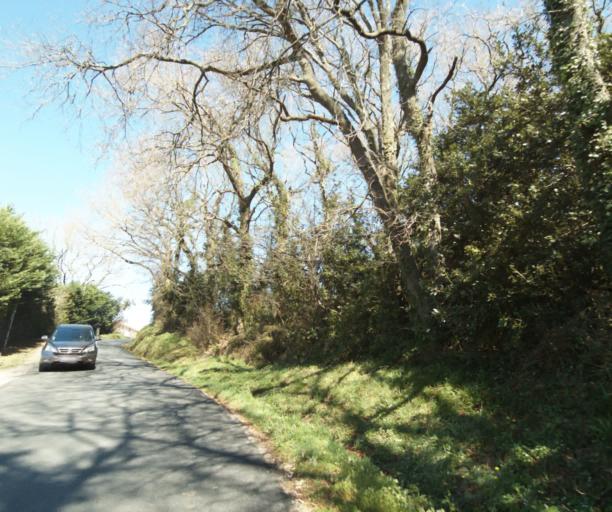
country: FR
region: Aquitaine
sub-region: Departement des Pyrenees-Atlantiques
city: Urrugne
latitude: 43.3487
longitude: -1.7141
